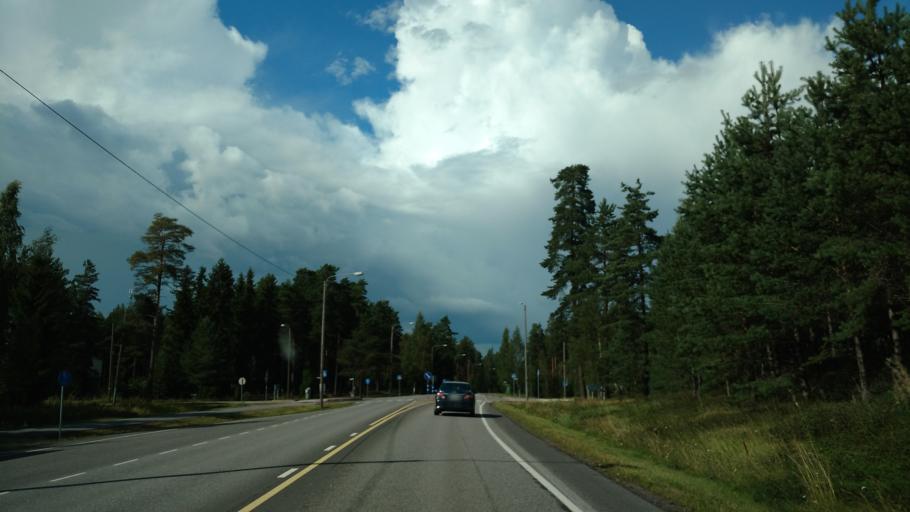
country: FI
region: Varsinais-Suomi
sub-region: Turku
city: Paimio
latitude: 60.4400
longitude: 22.7099
